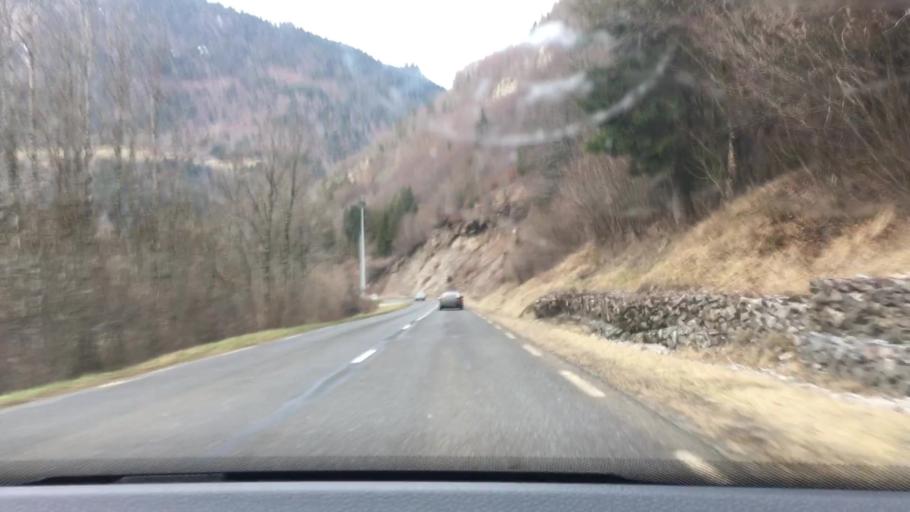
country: FR
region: Rhone-Alpes
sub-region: Departement de la Haute-Savoie
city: Abondance
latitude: 46.2932
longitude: 6.6835
